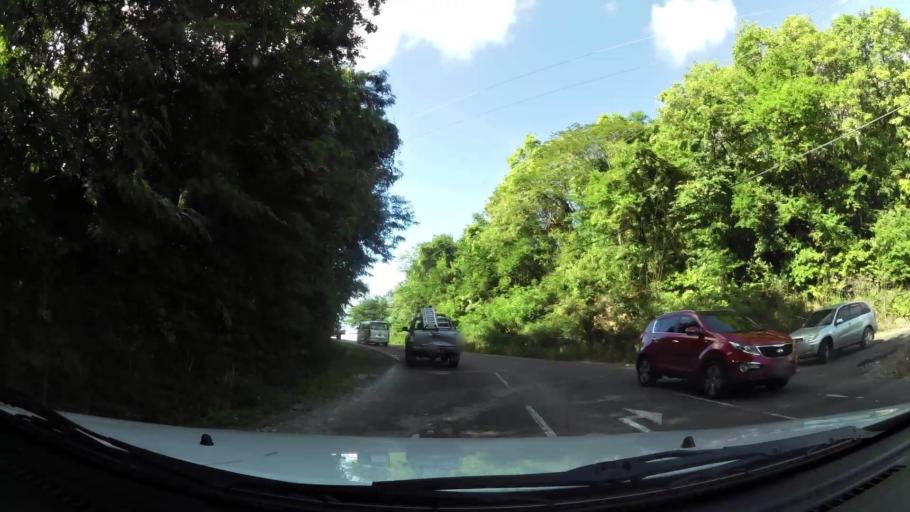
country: LC
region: Gros-Islet
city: Gros Islet
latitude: 14.0621
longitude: -60.9550
